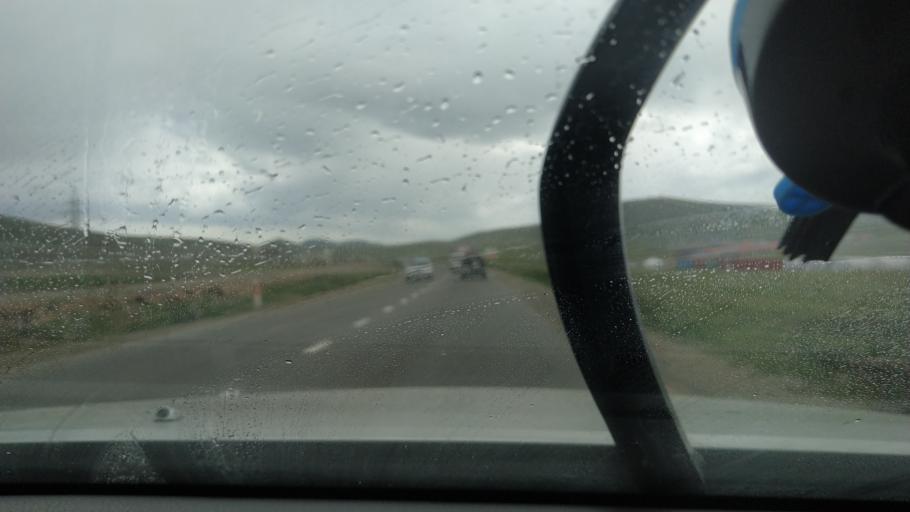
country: MN
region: Ulaanbaatar
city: Ulaanbaatar
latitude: 47.8017
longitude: 106.7471
